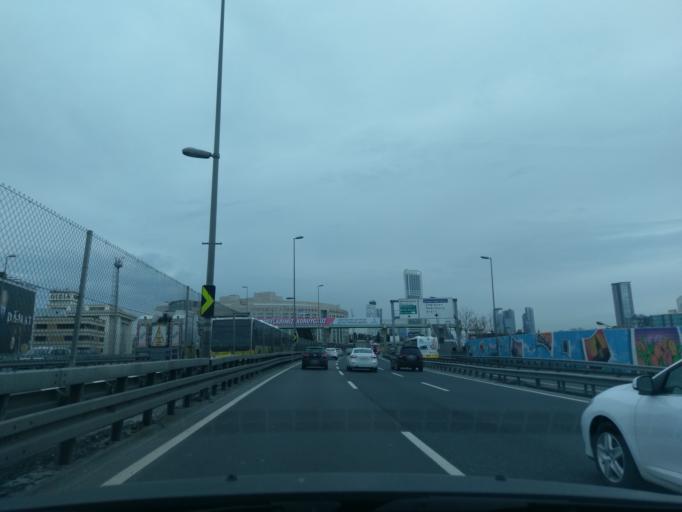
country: TR
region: Istanbul
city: Sisli
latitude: 41.0672
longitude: 28.9742
